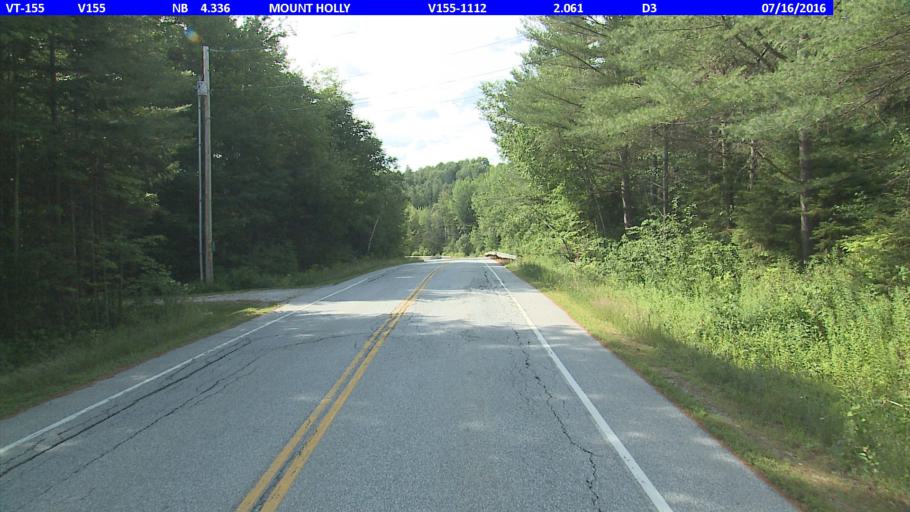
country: US
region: Vermont
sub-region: Windsor County
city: Chester
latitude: 43.3899
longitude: -72.8067
